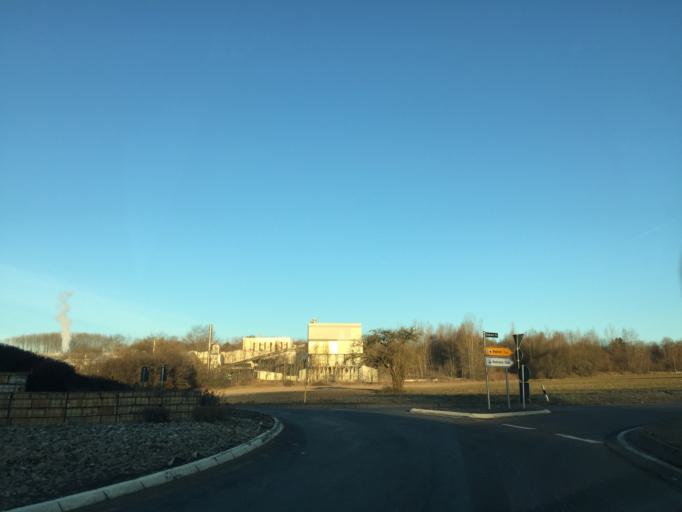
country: DE
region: Rheinland-Pfalz
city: Niederahr
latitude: 50.4758
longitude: 7.8604
